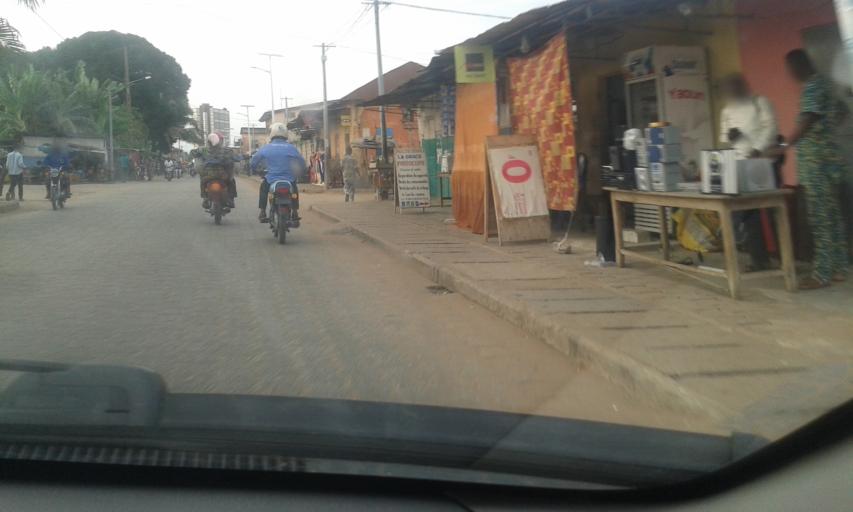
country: BJ
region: Queme
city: Porto-Novo
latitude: 6.4820
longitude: 2.6205
